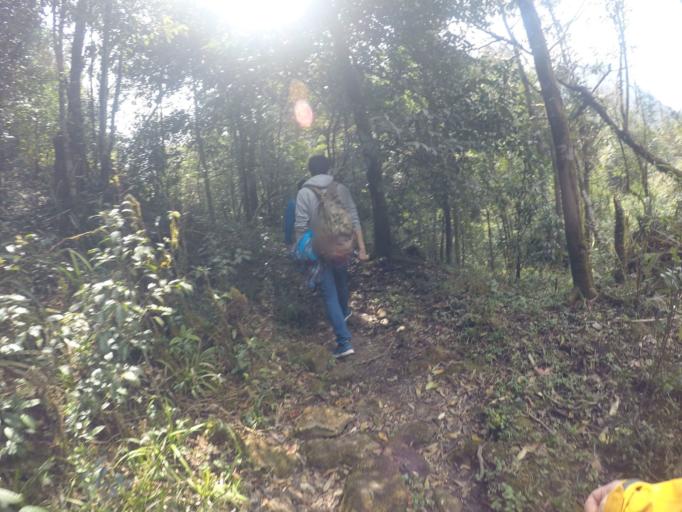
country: VN
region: Lao Cai
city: Sa Pa
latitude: 22.3508
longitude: 103.7728
